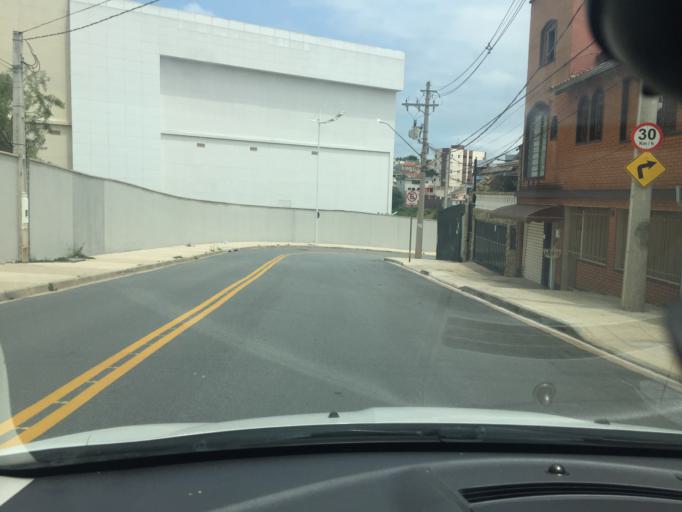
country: BR
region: Sao Paulo
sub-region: Jundiai
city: Jundiai
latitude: -23.1984
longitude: -46.8892
